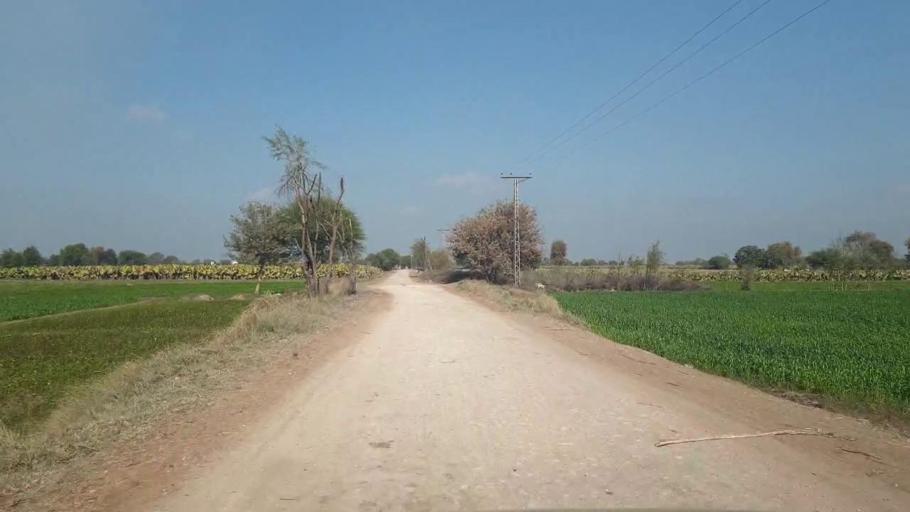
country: PK
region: Sindh
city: Shahdadpur
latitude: 25.9273
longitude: 68.5858
